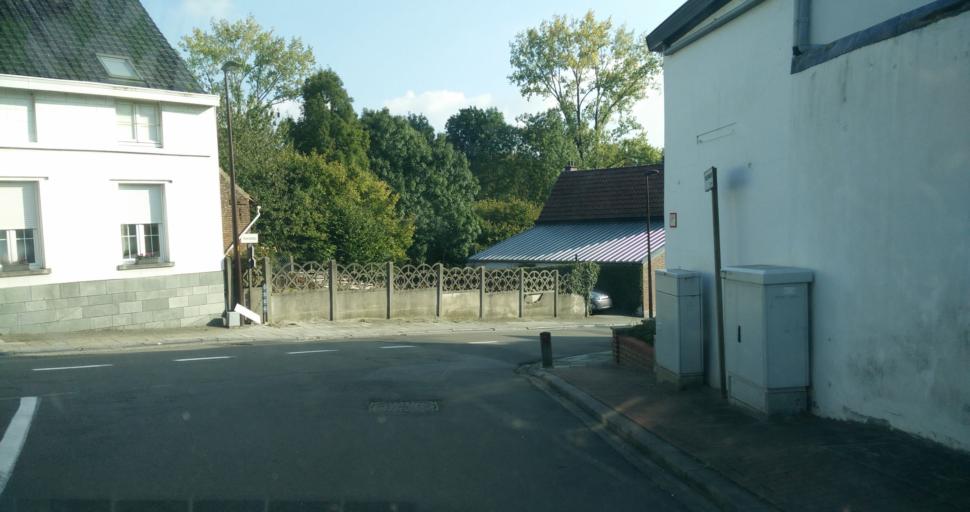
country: BE
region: Flanders
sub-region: Provincie Vlaams-Brabant
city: Beersel
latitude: 50.7494
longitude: 4.2803
